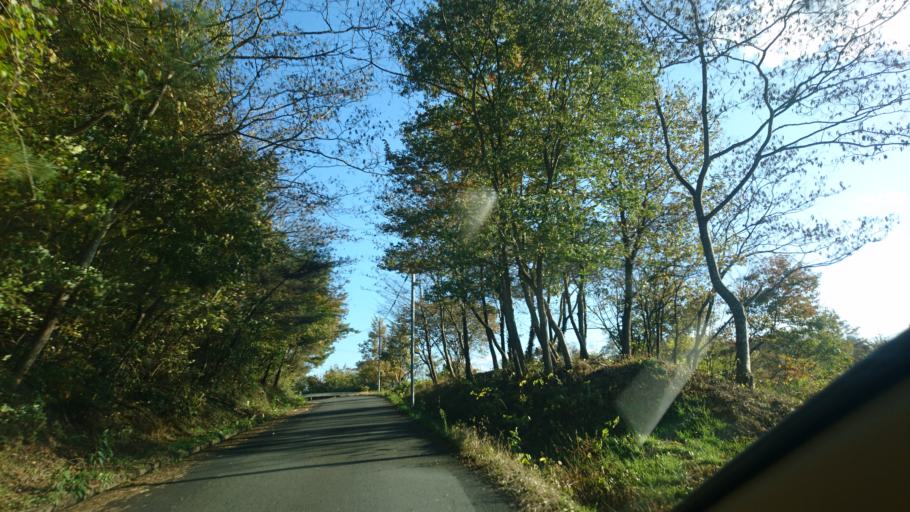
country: JP
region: Iwate
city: Ichinoseki
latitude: 38.9194
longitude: 141.2163
